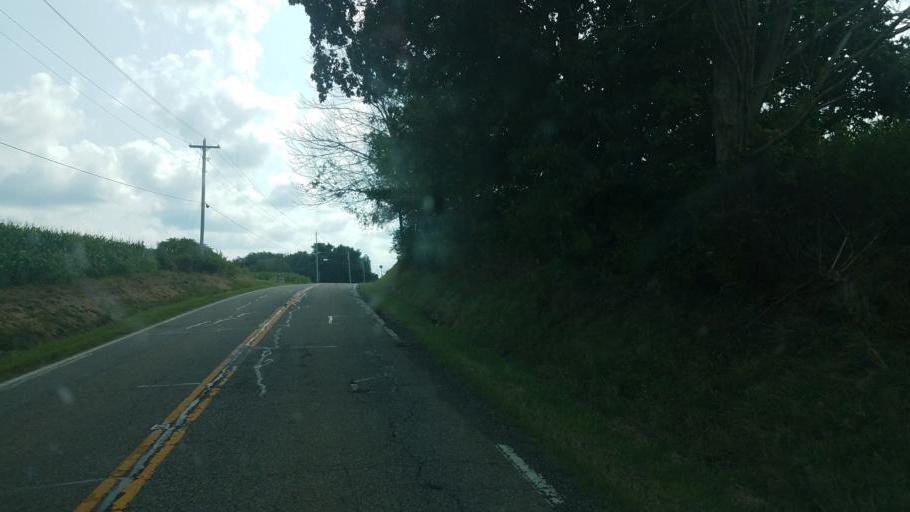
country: US
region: Ohio
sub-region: Stark County
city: Minerva
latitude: 40.7900
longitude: -81.0182
